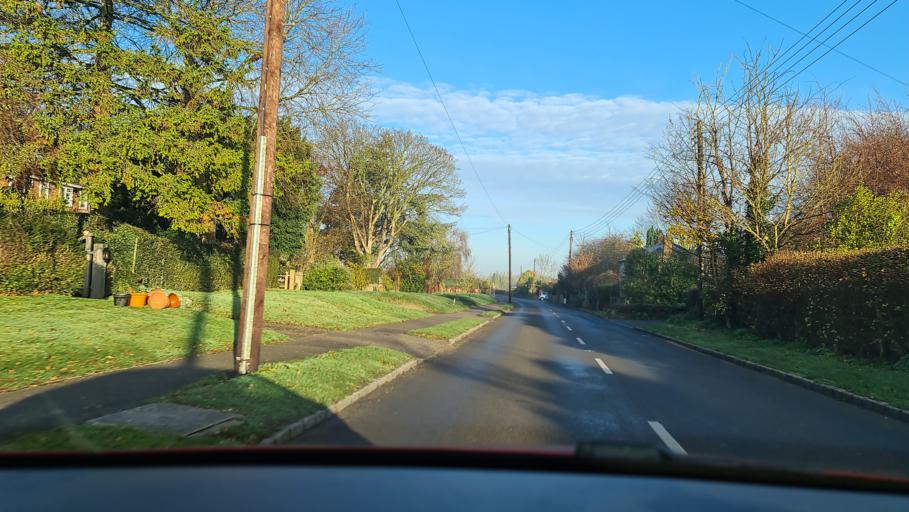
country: GB
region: England
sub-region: Buckinghamshire
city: Wendover
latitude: 51.7568
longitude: -0.7809
